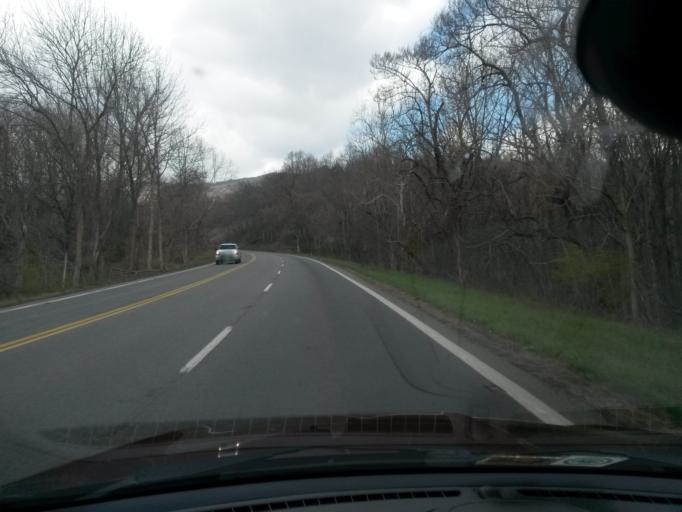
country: US
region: Virginia
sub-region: City of Waynesboro
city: Waynesboro
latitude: 38.0366
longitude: -78.8141
